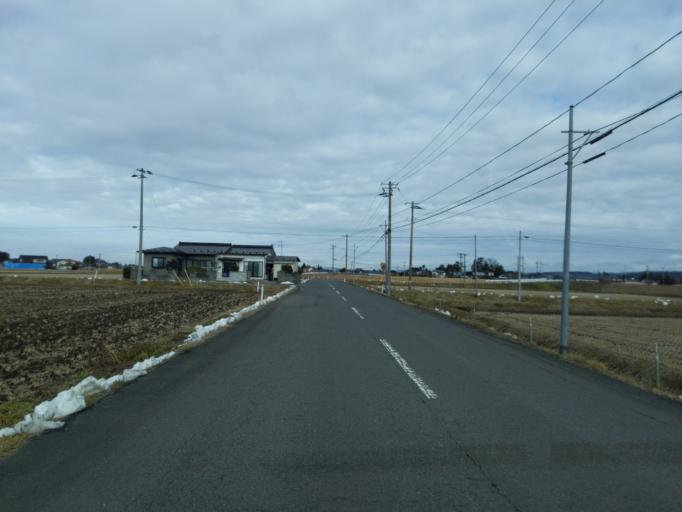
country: JP
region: Iwate
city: Mizusawa
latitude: 39.0801
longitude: 141.1653
